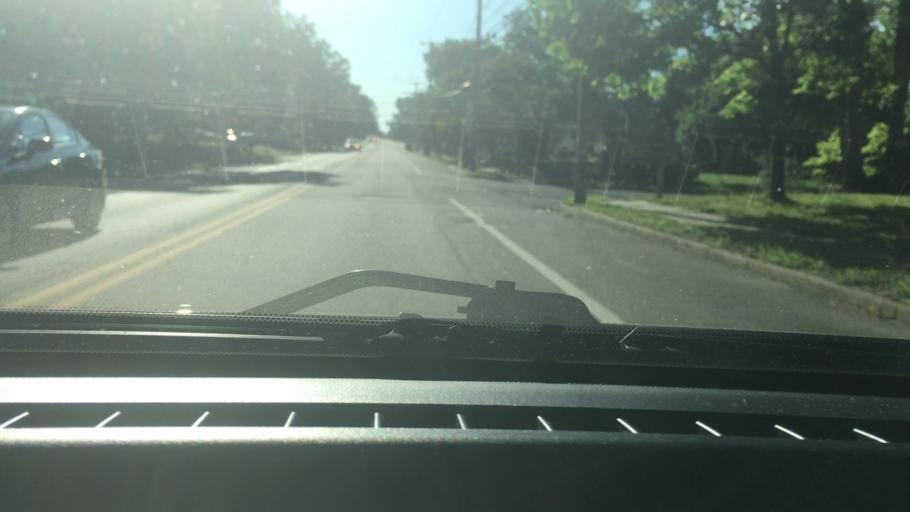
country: US
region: New Jersey
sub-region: Ocean County
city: Island Heights
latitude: 39.9700
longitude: -74.1473
